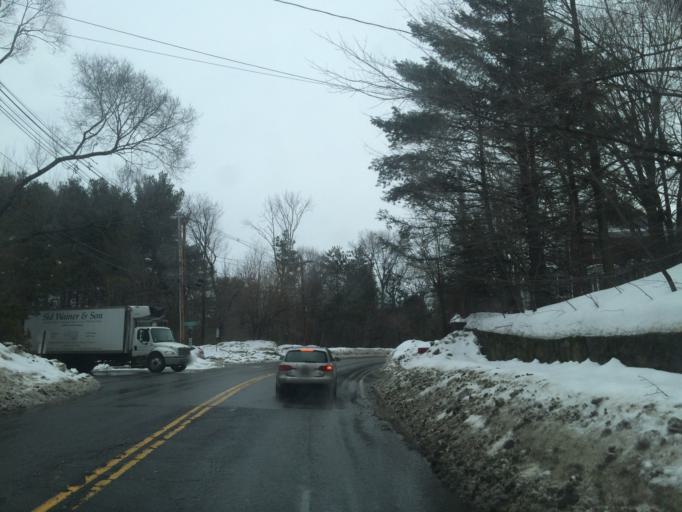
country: US
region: Massachusetts
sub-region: Middlesex County
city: Weston
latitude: 42.3801
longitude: -71.2783
